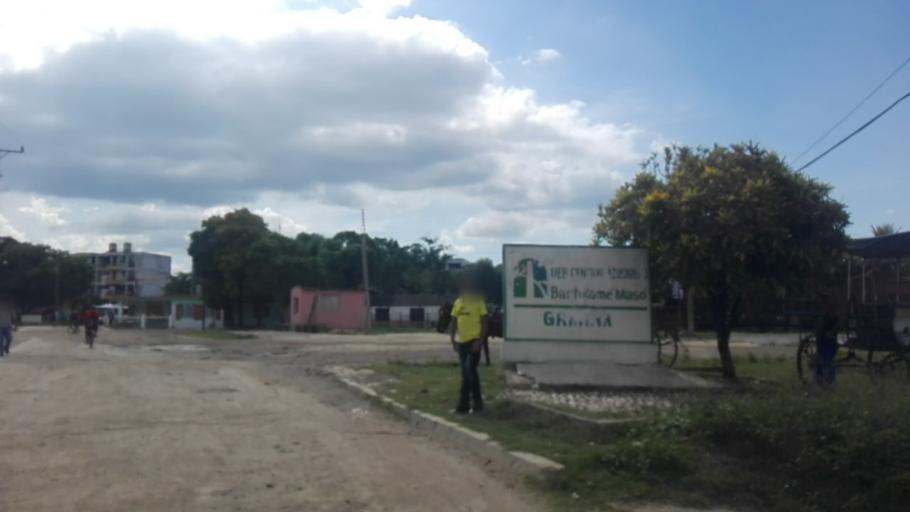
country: CU
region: Granma
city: Bartolome Maso
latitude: 20.1667
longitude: -76.9440
